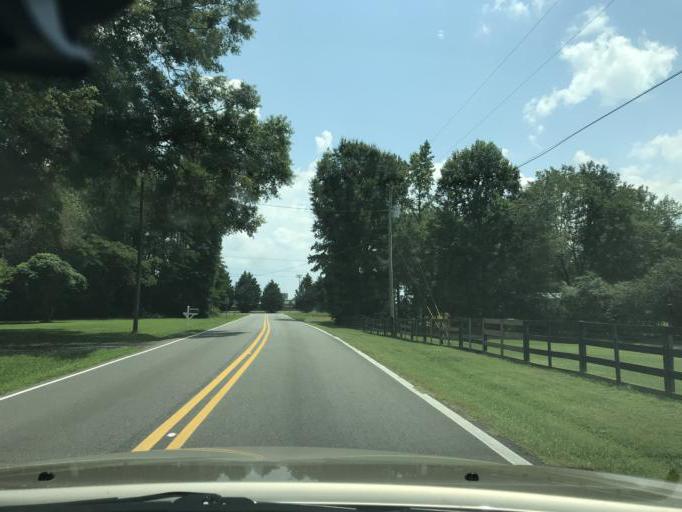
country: US
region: Georgia
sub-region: Forsyth County
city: Cumming
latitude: 34.2593
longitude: -84.2193
